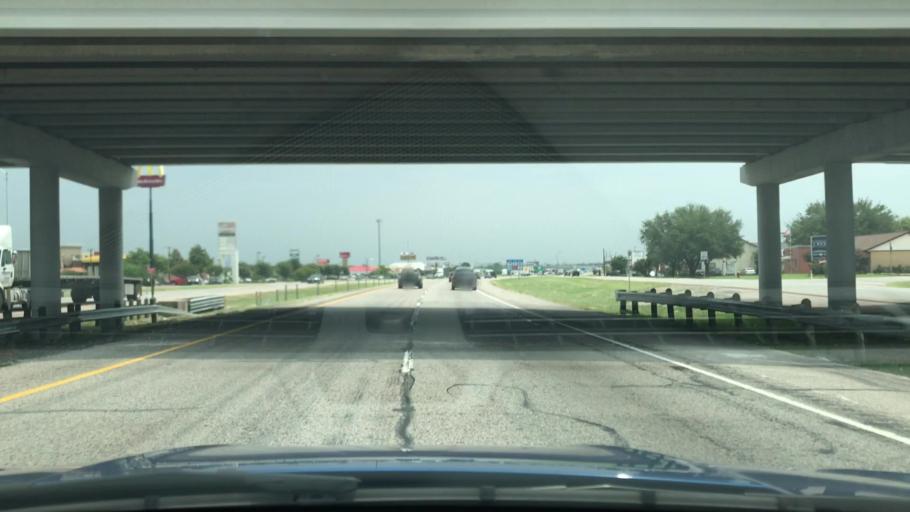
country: US
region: Texas
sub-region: Kaufman County
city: Forney
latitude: 32.7561
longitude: -96.4682
